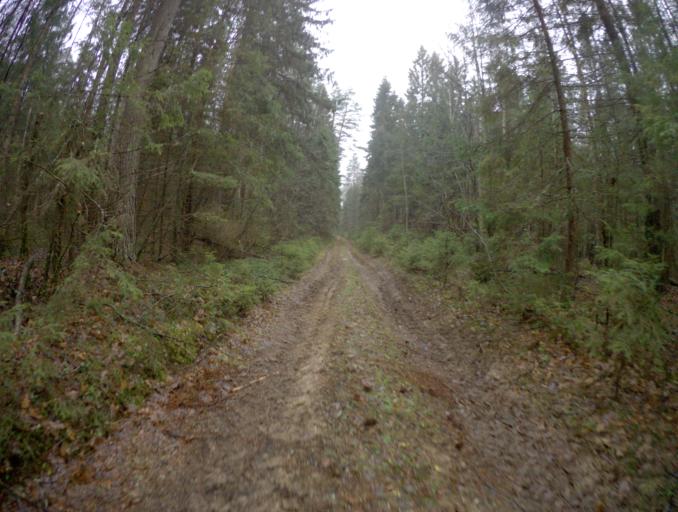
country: RU
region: Vladimir
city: Golovino
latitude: 56.0051
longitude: 40.4747
